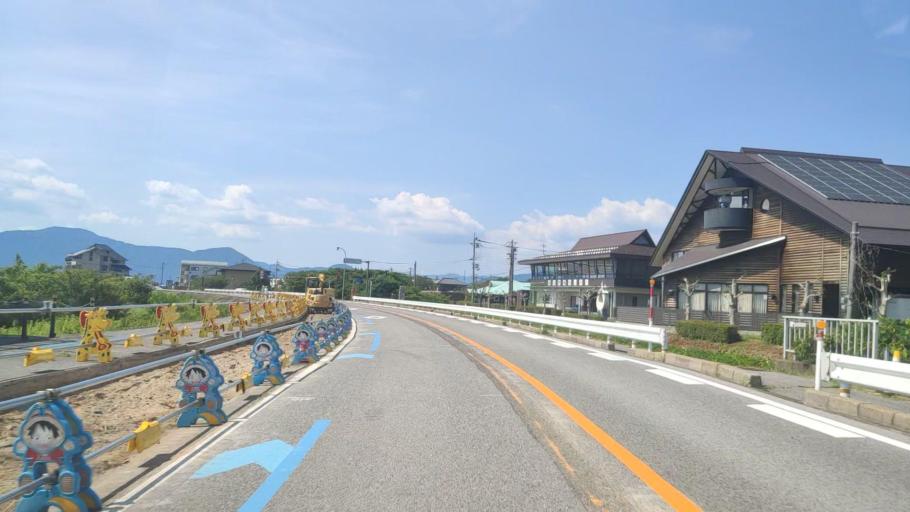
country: JP
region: Shiga Prefecture
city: Nagahama
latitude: 35.4458
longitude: 136.1897
